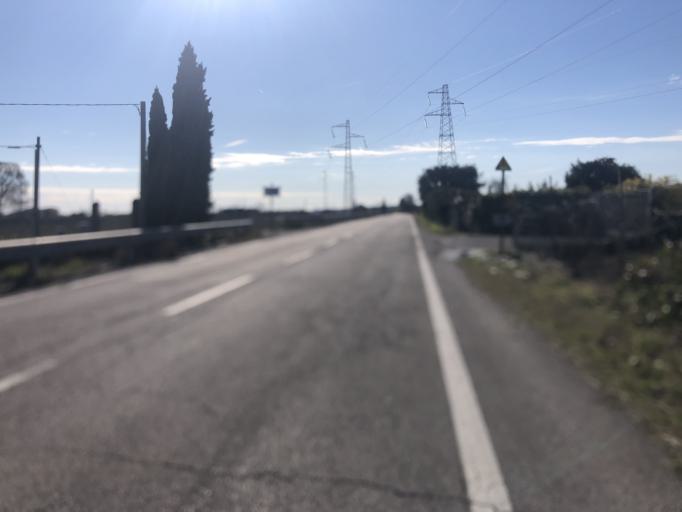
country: IT
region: Veneto
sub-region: Provincia di Verona
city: Ospedaletto
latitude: 45.4967
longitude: 10.8414
